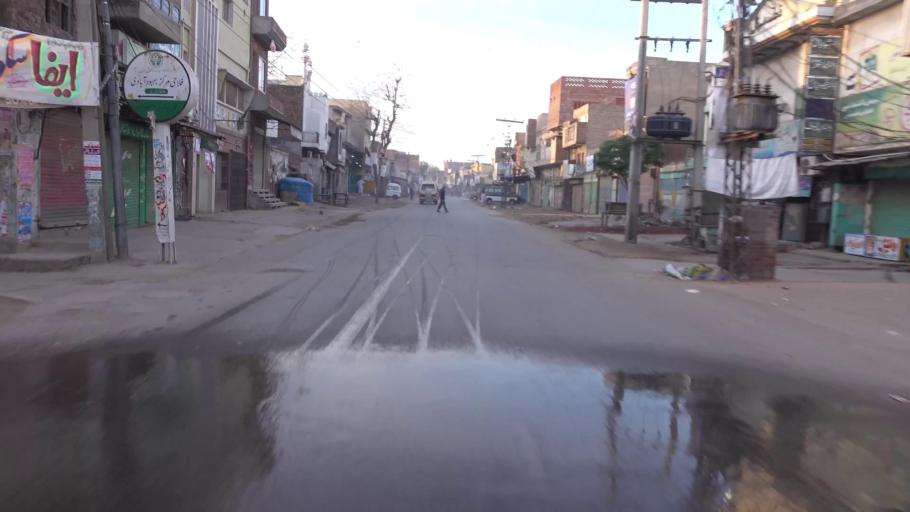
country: PK
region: Punjab
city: Hafizabad
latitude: 32.0685
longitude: 73.6889
